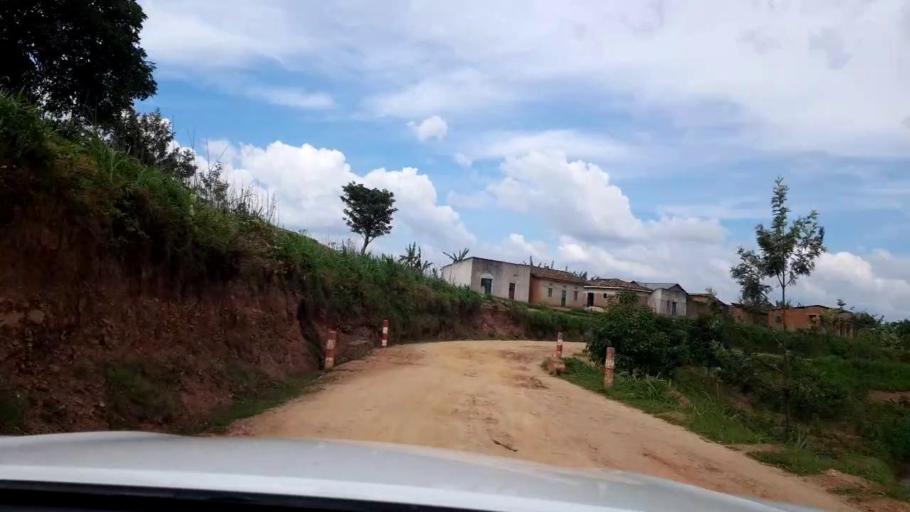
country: RW
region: Southern Province
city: Gitarama
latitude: -1.9846
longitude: 29.7088
